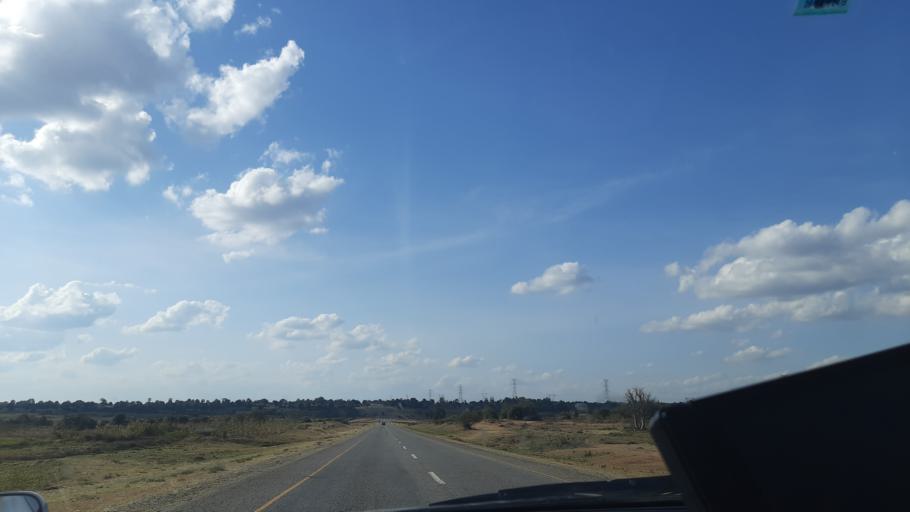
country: TZ
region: Singida
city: Ikungi
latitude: -5.1008
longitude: 34.7655
